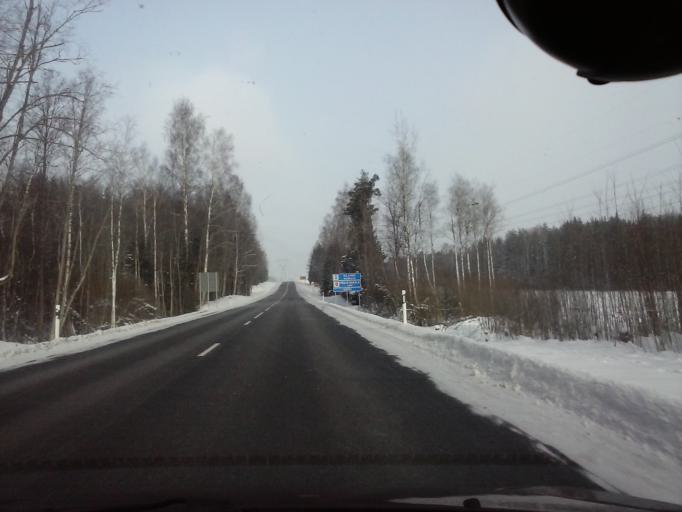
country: EE
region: Viljandimaa
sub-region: Abja vald
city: Abja-Paluoja
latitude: 58.2698
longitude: 25.2640
